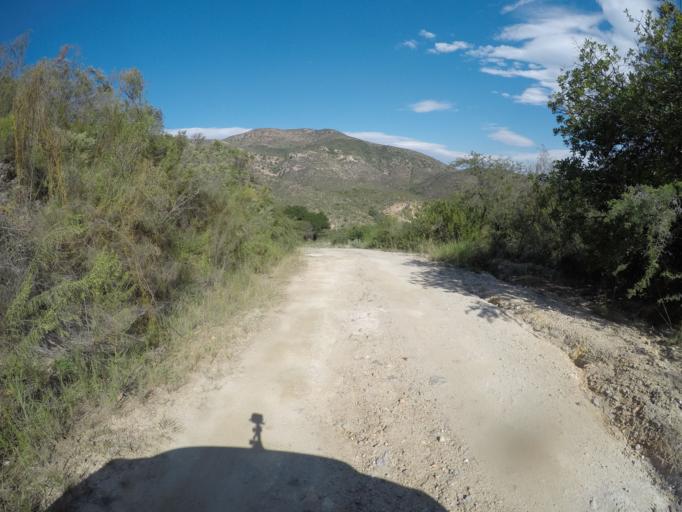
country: ZA
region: Eastern Cape
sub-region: Cacadu District Municipality
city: Kareedouw
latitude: -33.6456
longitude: 24.4566
